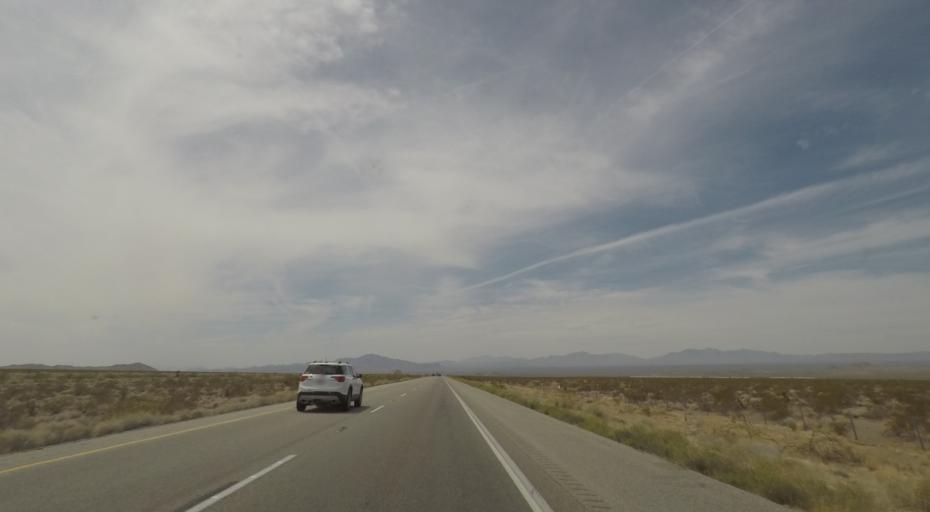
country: US
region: California
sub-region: San Bernardino County
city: Needles
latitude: 34.8245
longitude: -115.0945
